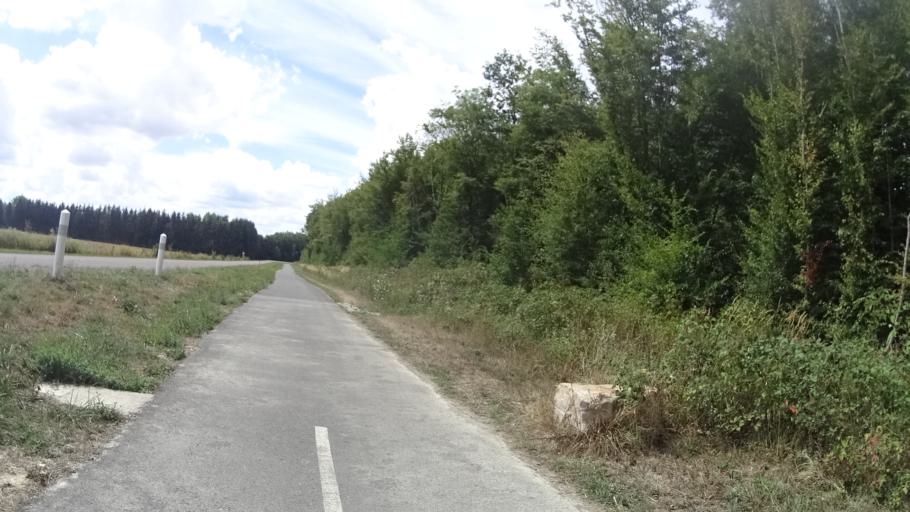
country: FR
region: Franche-Comte
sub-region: Departement du Jura
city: Damparis
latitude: 47.0776
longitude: 5.3912
